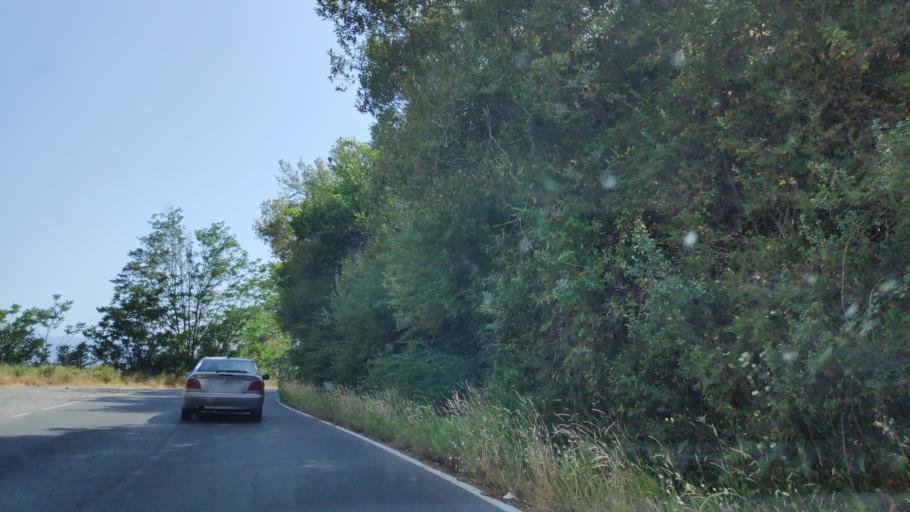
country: ES
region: Andalusia
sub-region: Provincia de Granada
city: Pampaneira
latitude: 36.9361
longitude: -3.3681
